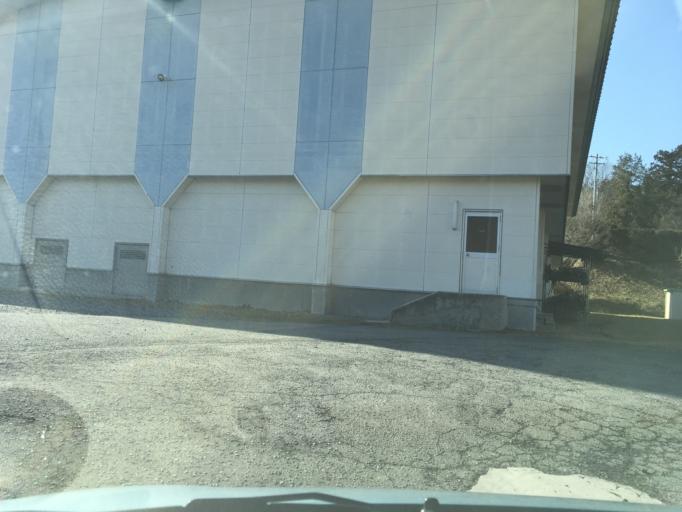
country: JP
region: Iwate
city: Ichinoseki
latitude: 38.8523
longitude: 141.2913
